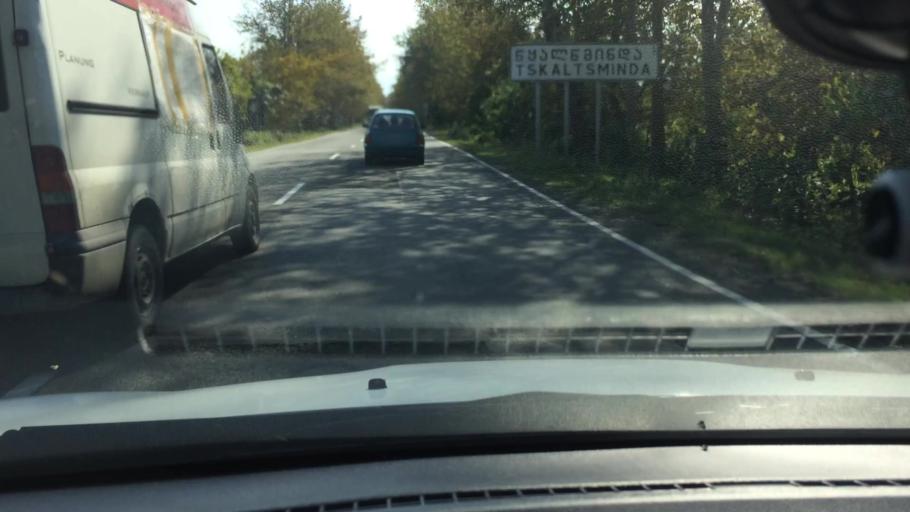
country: GE
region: Guria
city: Urek'i
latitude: 42.0157
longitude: 41.7703
